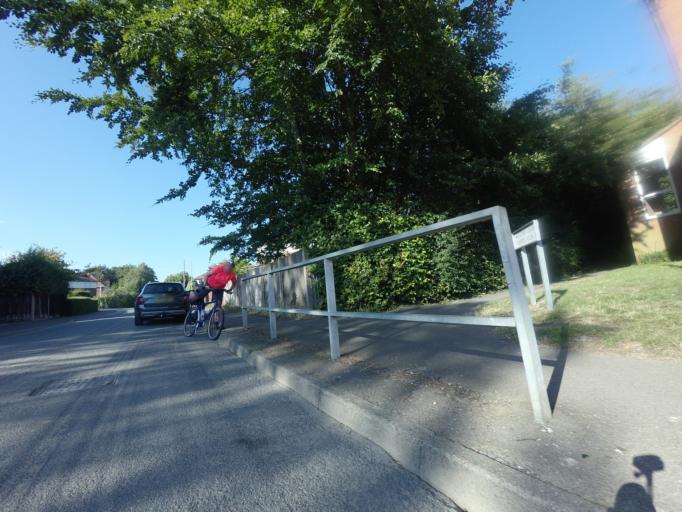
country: GB
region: England
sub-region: Kent
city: Tenterden
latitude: 51.0677
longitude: 0.7011
